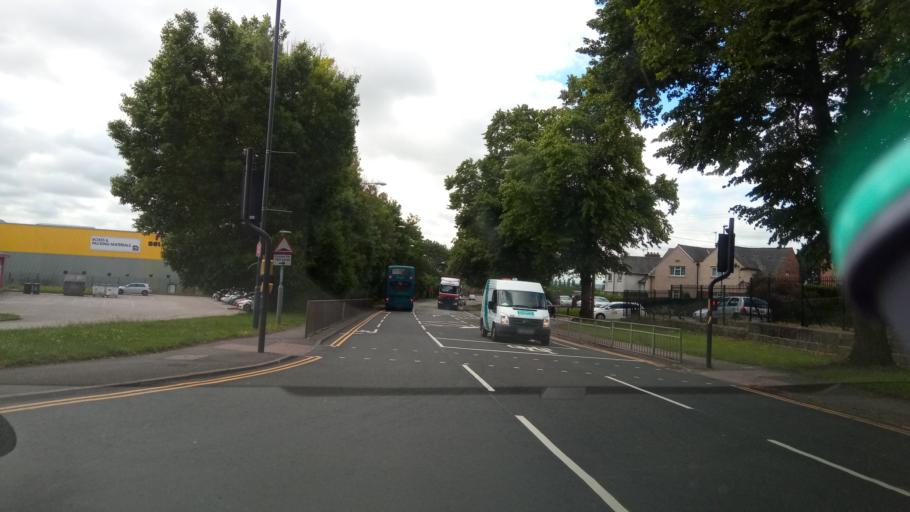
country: GB
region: England
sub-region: Derby
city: Derby
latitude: 52.8961
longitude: -1.4790
